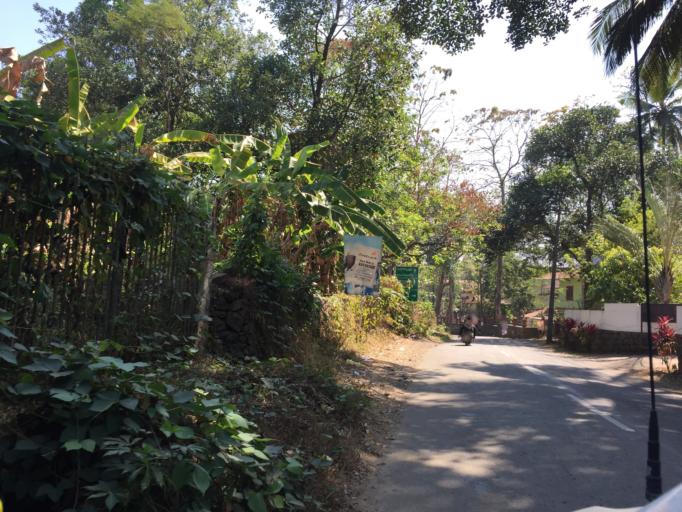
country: IN
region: Kerala
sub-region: Kottayam
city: Erattupetta
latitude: 9.6839
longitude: 76.7719
